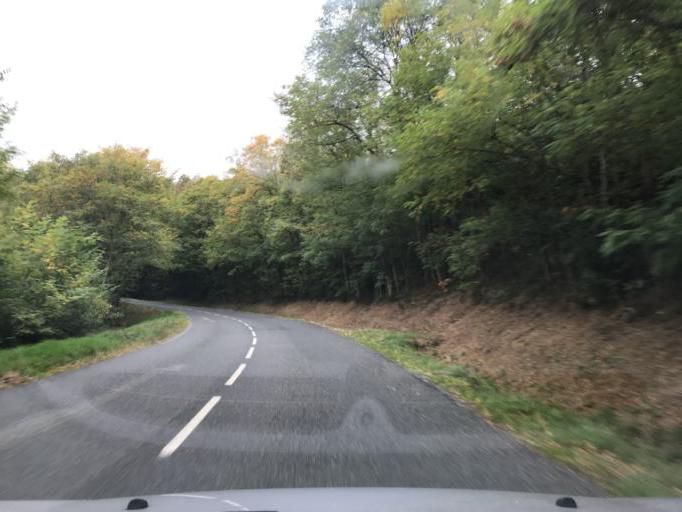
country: FR
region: Rhone-Alpes
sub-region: Departement du Rhone
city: Le Perreon
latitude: 46.0184
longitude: 4.5750
